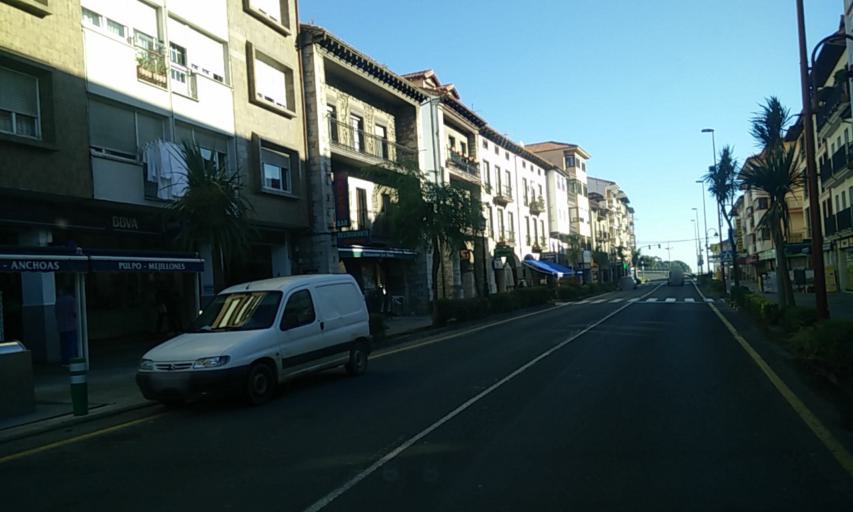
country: ES
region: Cantabria
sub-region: Provincia de Cantabria
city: San Vicente de la Barquera
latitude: 43.3846
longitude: -4.3995
